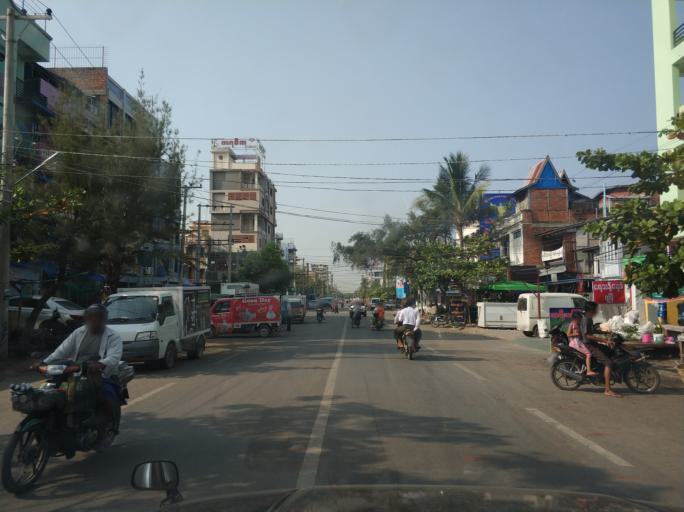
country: MM
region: Mandalay
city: Mandalay
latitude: 21.9694
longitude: 96.0914
